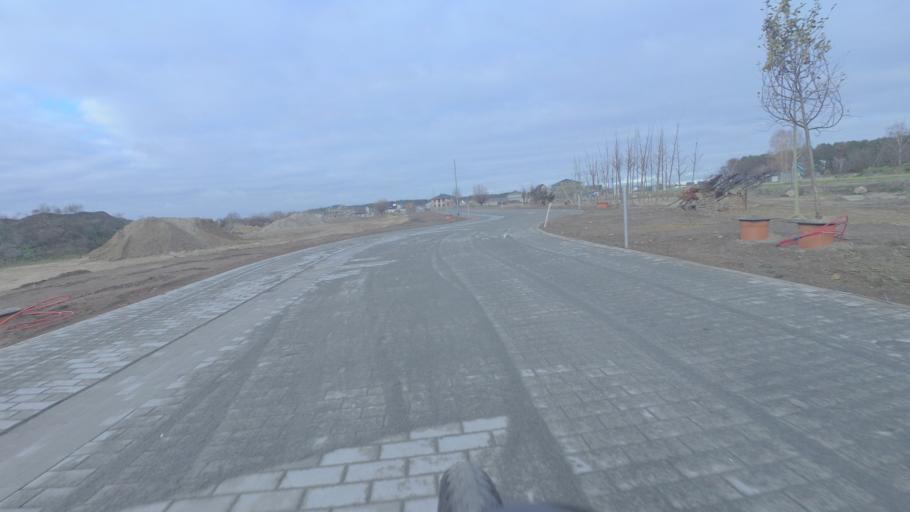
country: DE
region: Brandenburg
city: Ludwigsfelde
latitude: 52.3084
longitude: 13.2105
